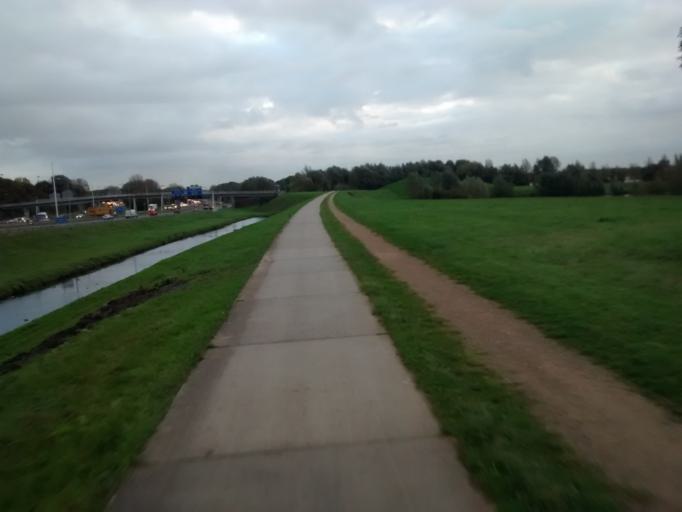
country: NL
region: Utrecht
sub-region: Gemeente Utrecht
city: Lunetten
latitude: 52.0546
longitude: 5.1275
